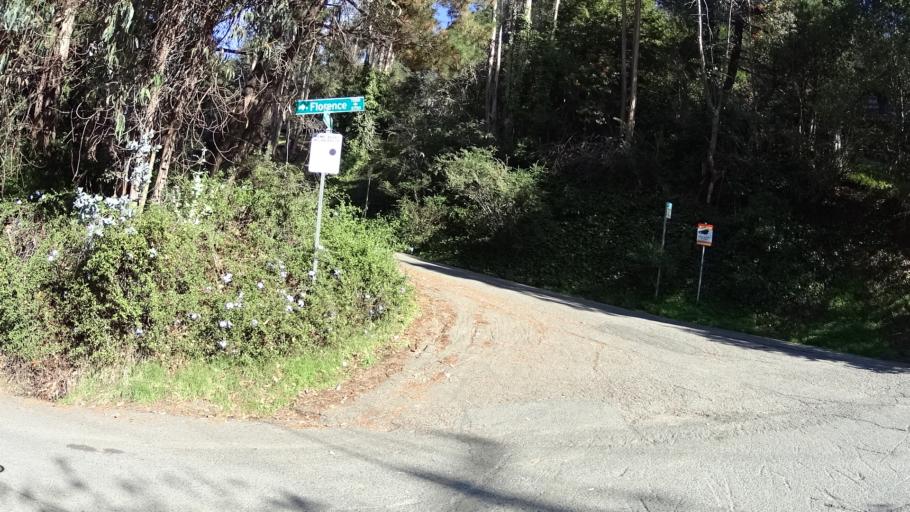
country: US
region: California
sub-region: Alameda County
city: Piedmont
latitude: 37.8364
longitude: -122.2159
